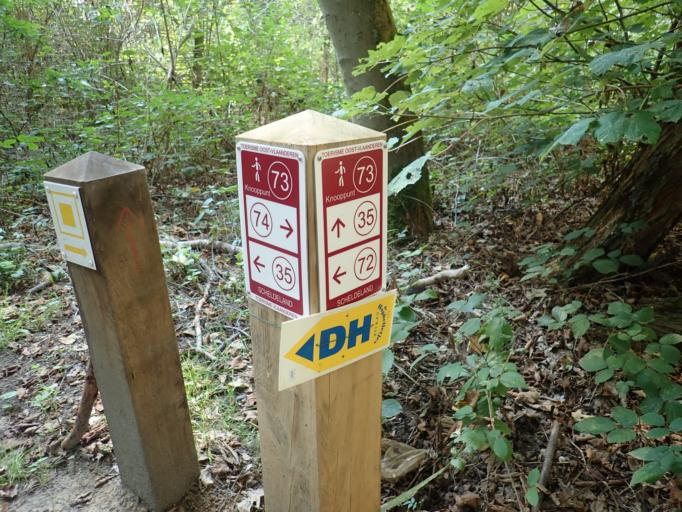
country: BE
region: Flanders
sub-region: Provincie Vlaams-Brabant
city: Opwijk
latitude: 50.9379
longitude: 4.1558
